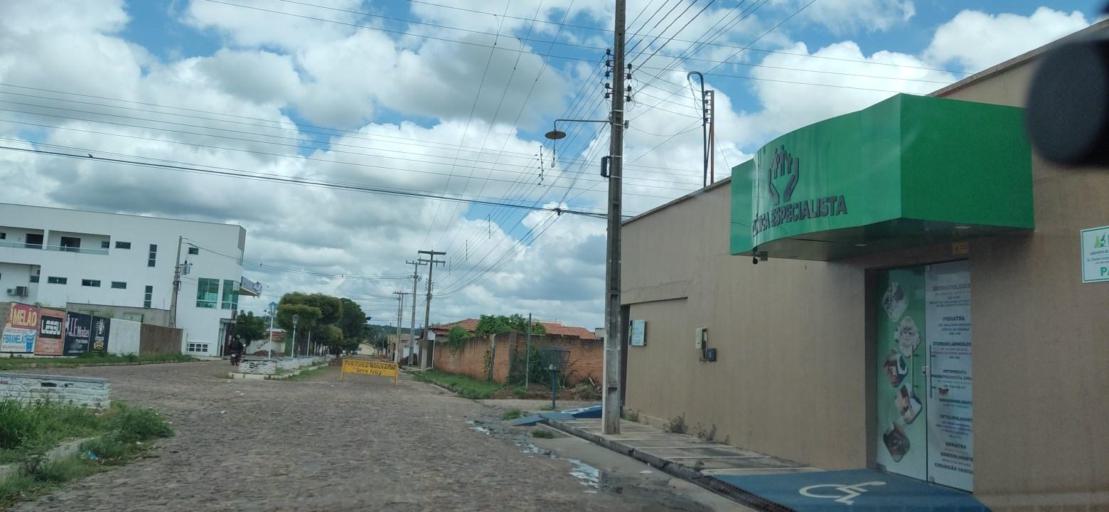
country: BR
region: Piaui
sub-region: Valenca Do Piaui
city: Valenca do Piaui
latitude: -6.4002
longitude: -41.7375
